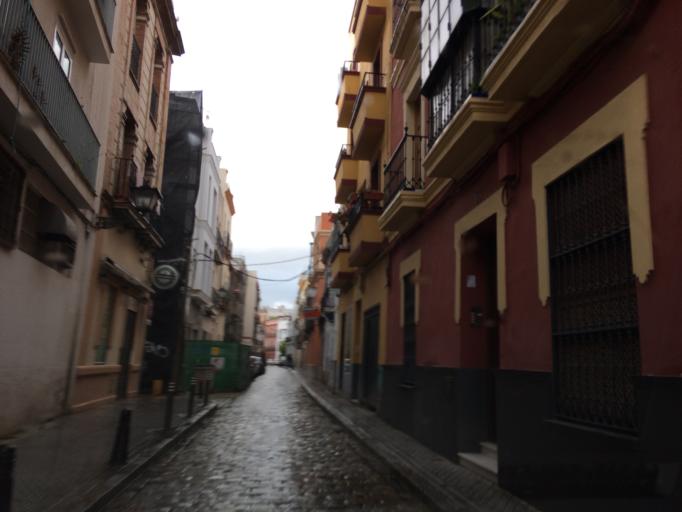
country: ES
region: Andalusia
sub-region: Provincia de Sevilla
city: Sevilla
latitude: 37.3977
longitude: -5.9931
